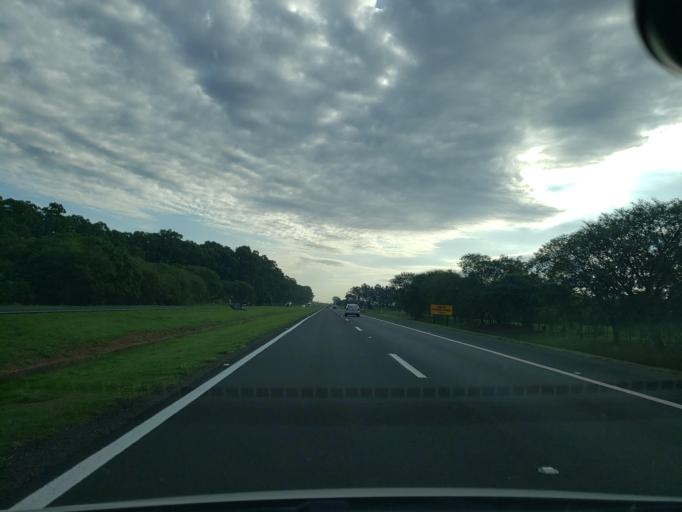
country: BR
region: Sao Paulo
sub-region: Guararapes
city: Guararapes
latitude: -21.2147
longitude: -50.6949
